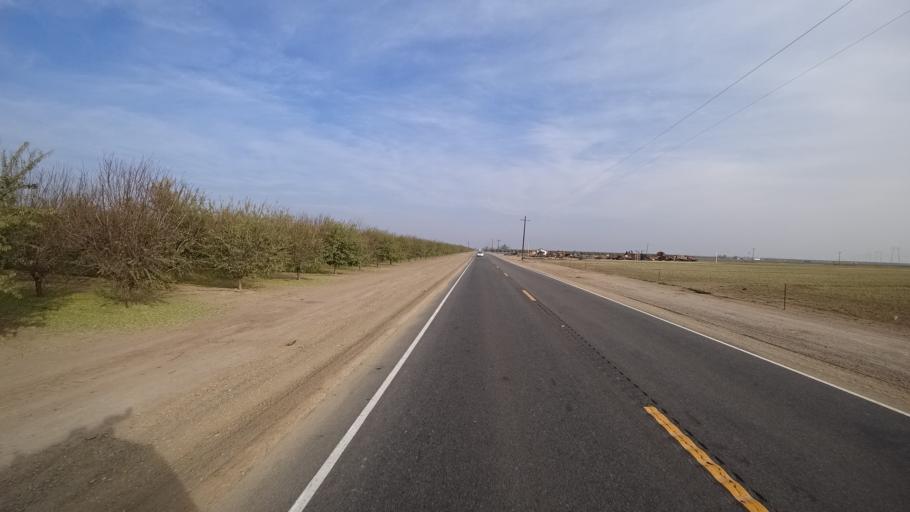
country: US
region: California
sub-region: Kern County
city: Rosedale
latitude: 35.2672
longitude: -119.1400
